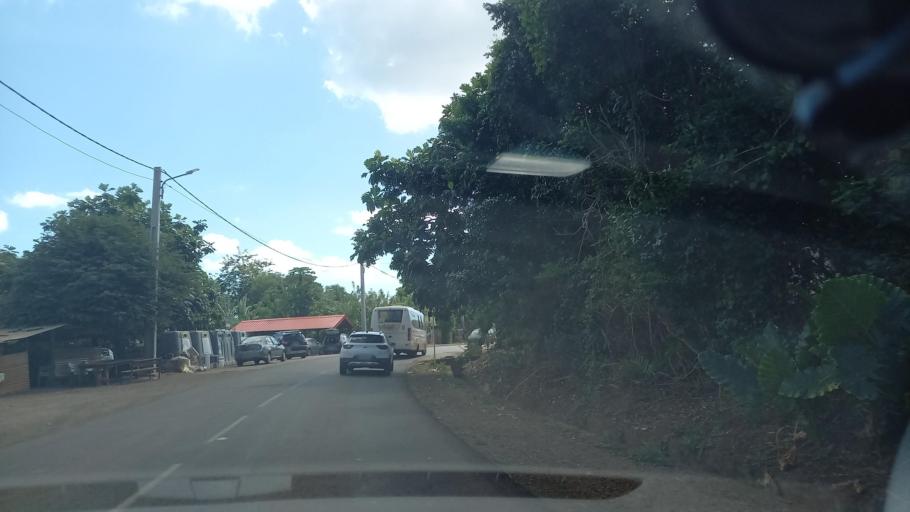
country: YT
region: Chirongui
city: Chirongui
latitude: -12.9060
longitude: 45.1516
